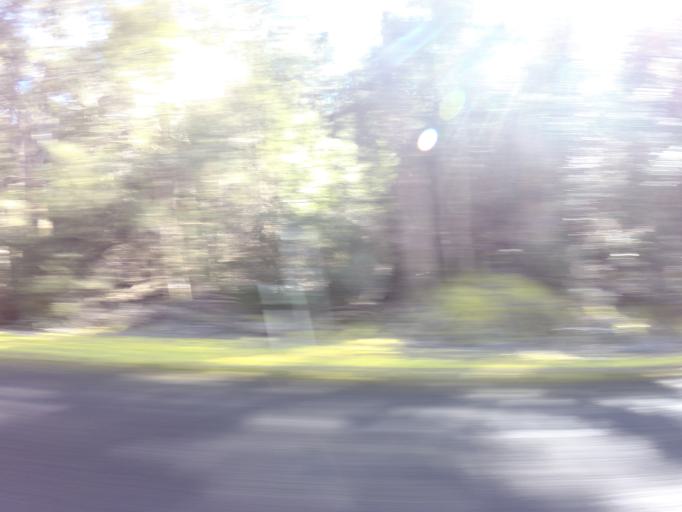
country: AU
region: Tasmania
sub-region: Derwent Valley
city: New Norfolk
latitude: -42.7682
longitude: 146.5627
